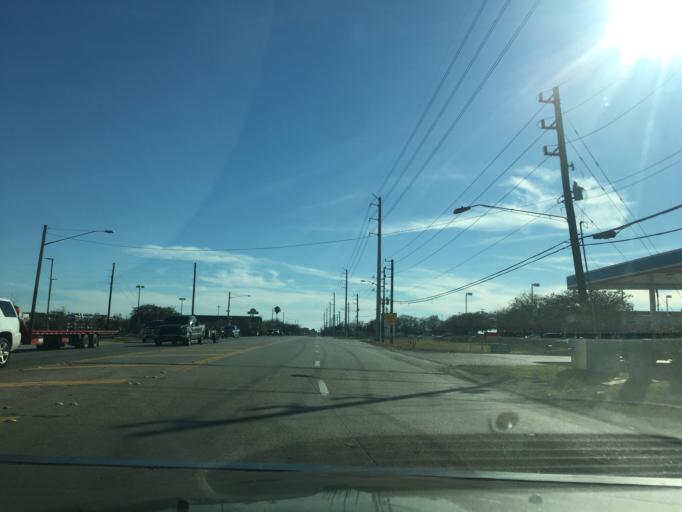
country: US
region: Texas
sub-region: Fort Bend County
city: Rosenberg
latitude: 29.5315
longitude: -95.8083
